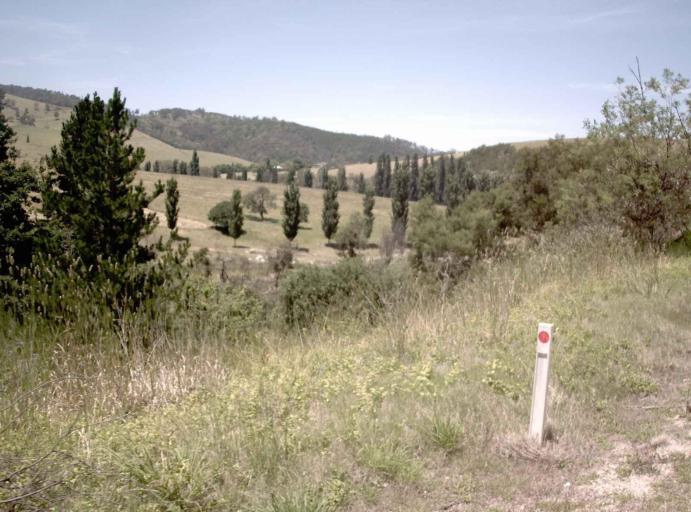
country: AU
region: Victoria
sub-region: East Gippsland
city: Bairnsdale
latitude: -37.5045
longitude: 147.8405
